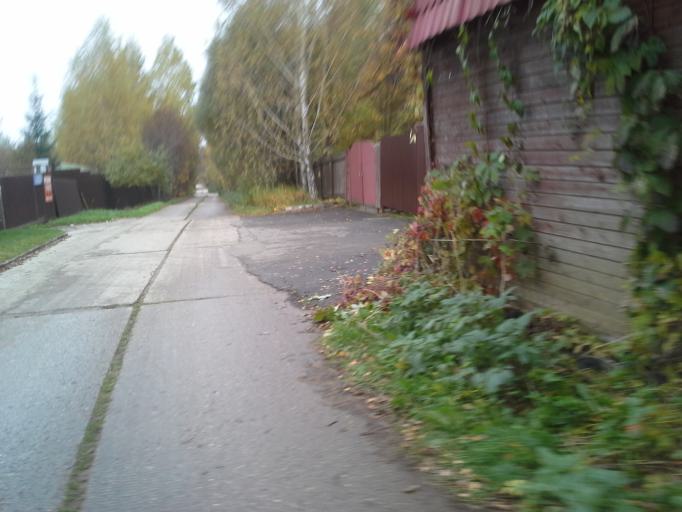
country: RU
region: Moskovskaya
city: Nazar'yevo
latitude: 55.6816
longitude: 37.0069
